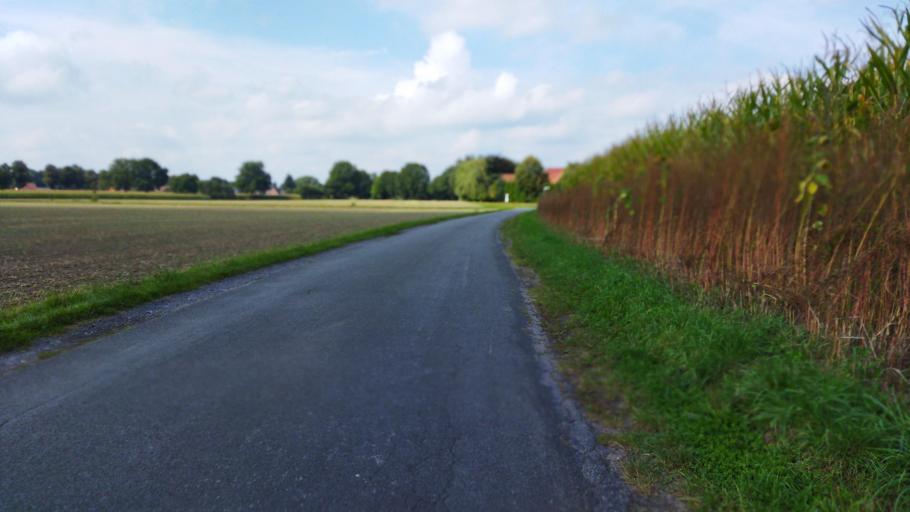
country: DE
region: North Rhine-Westphalia
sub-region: Regierungsbezirk Munster
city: Warendorf
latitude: 51.9576
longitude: 7.9613
